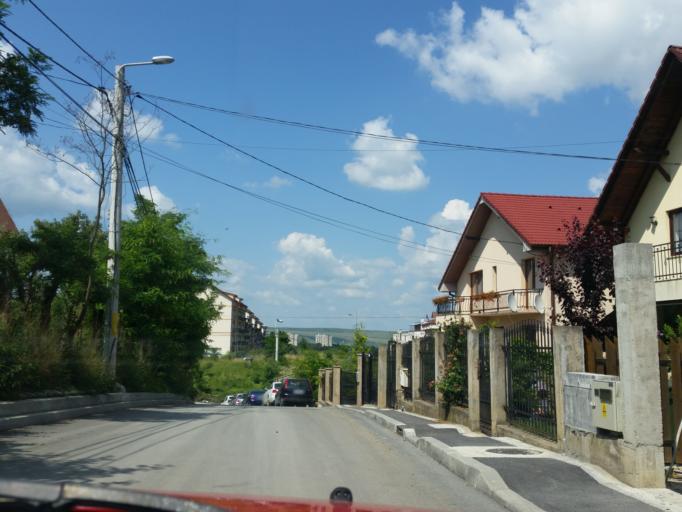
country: RO
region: Cluj
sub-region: Municipiul Cluj-Napoca
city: Cluj-Napoca
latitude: 46.7542
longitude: 23.6208
